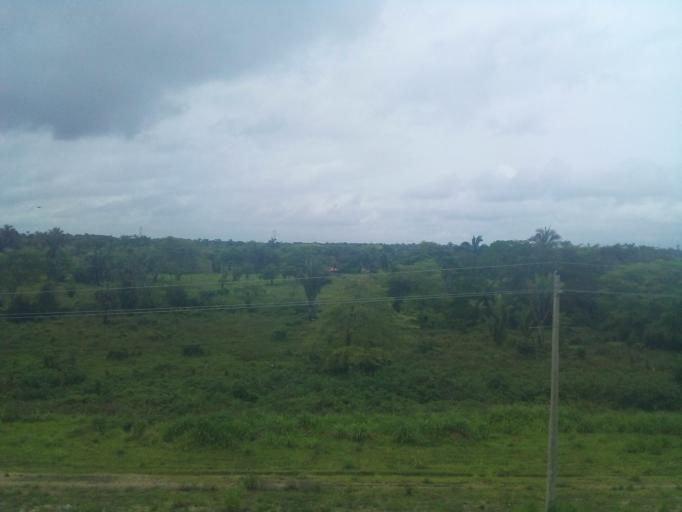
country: BR
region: Maranhao
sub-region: Vitoria Do Mearim
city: Vitoria do Mearim
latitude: -3.5485
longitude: -44.8295
